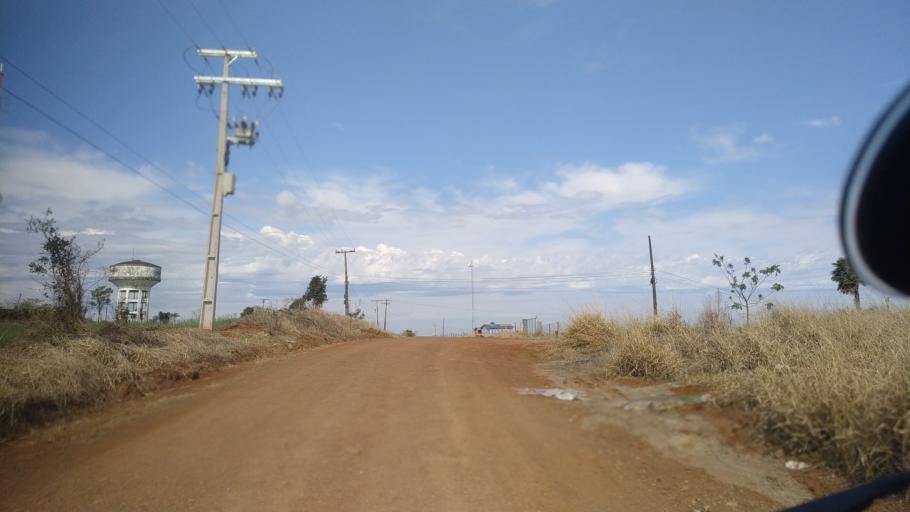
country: BR
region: Santa Catarina
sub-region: Chapeco
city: Chapeco
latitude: -27.1175
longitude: -52.5872
